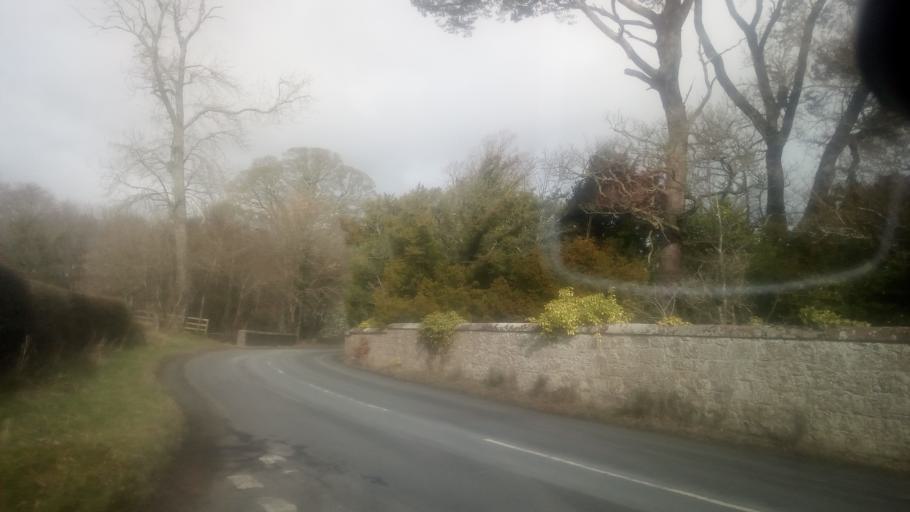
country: GB
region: Scotland
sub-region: The Scottish Borders
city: Melrose
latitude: 55.5950
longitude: -2.7380
